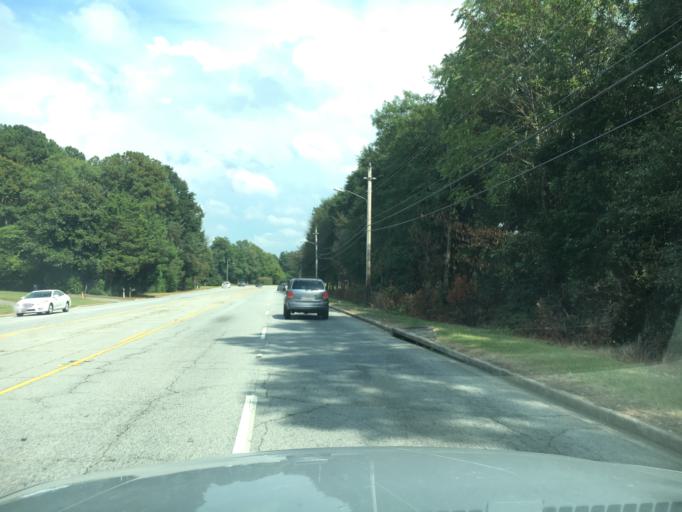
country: US
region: South Carolina
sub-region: Greenville County
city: Wade Hampton
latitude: 34.8586
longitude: -82.3323
